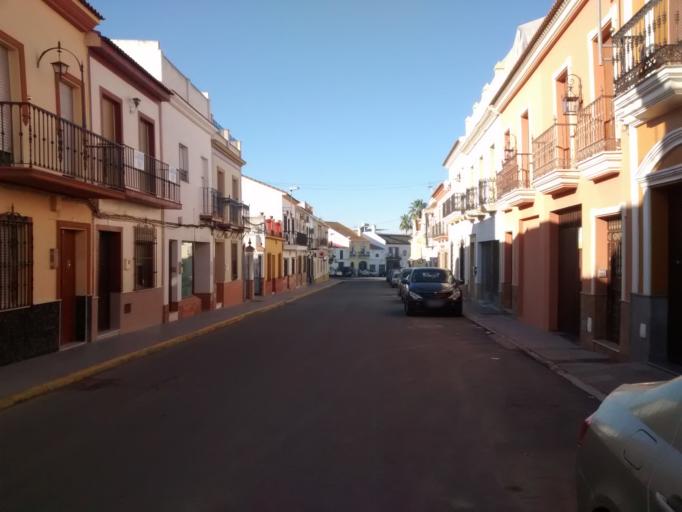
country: ES
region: Andalusia
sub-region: Provincia de Huelva
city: Bollullos par del Condado
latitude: 37.3091
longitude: -6.5999
